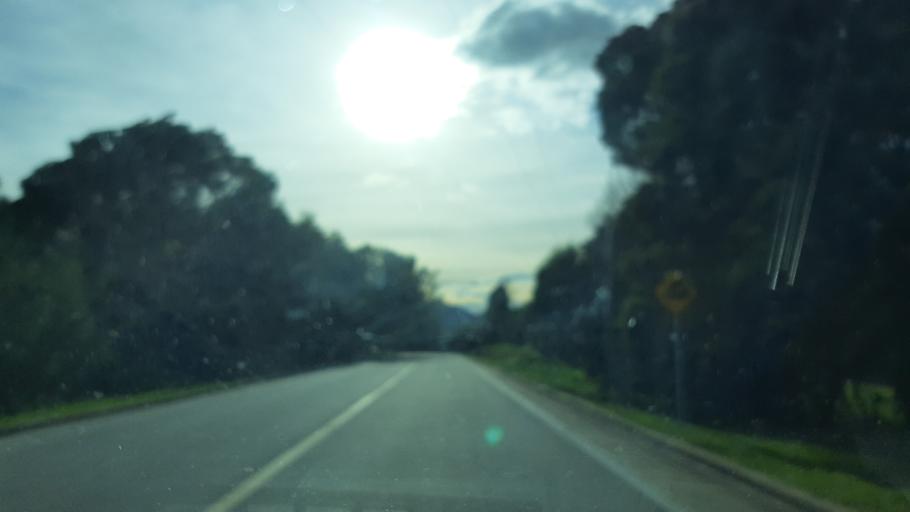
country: CO
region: Cundinamarca
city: Choconta
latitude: 5.0976
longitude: -73.6941
